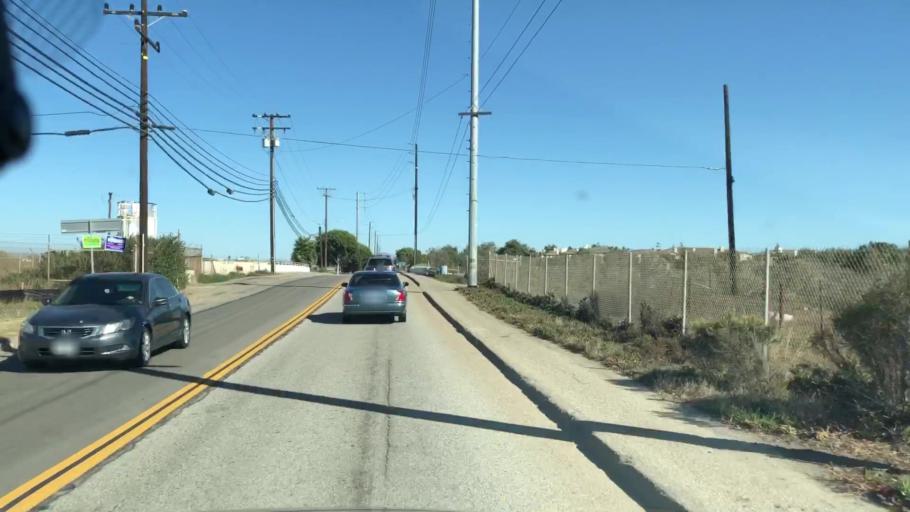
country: US
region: California
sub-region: Ventura County
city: Oxnard Shores
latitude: 34.1905
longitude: -119.2352
